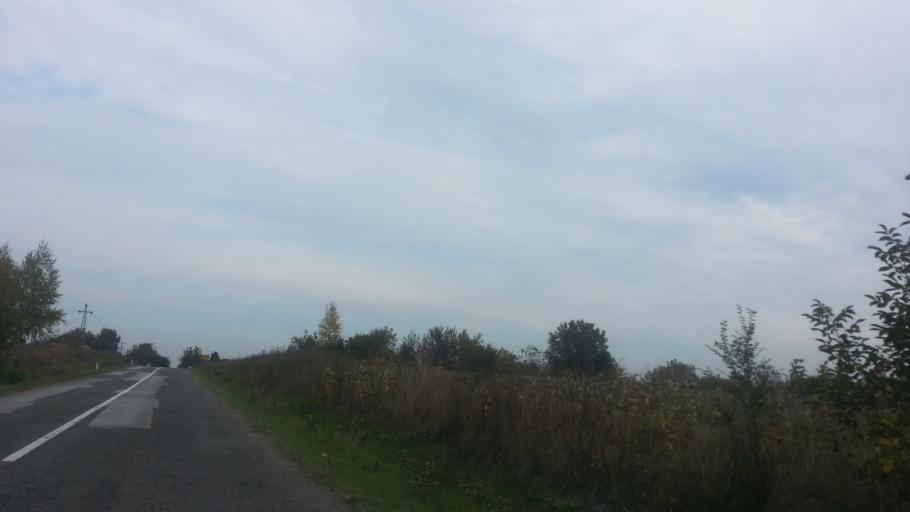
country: RS
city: Surduk
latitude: 45.0602
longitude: 20.3307
